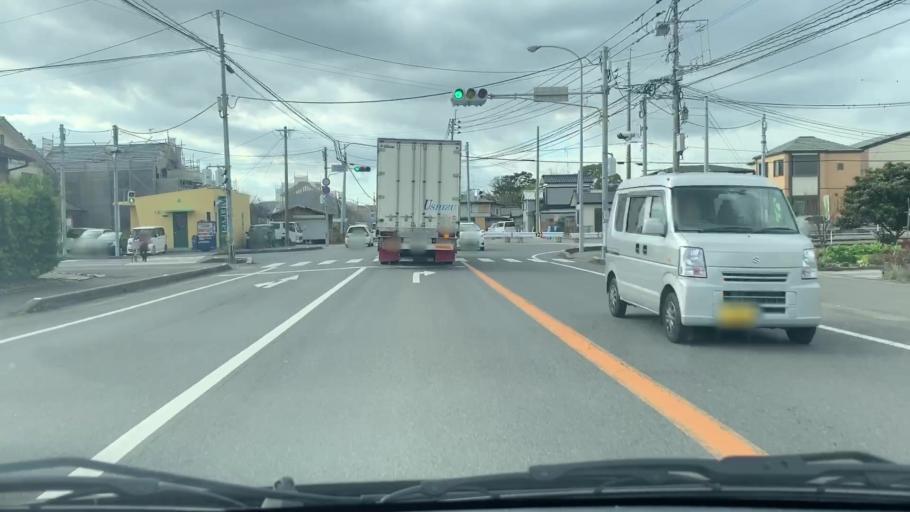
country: JP
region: Saga Prefecture
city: Saga-shi
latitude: 33.2494
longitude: 130.2292
